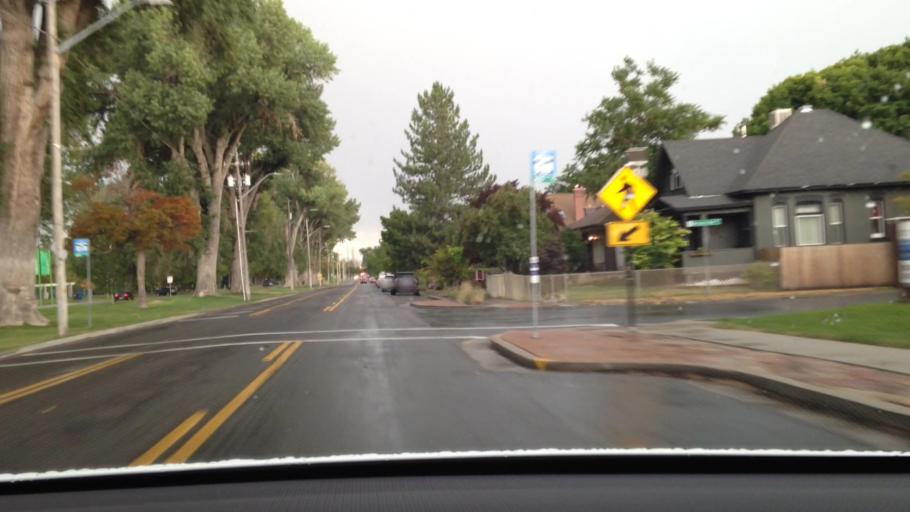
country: US
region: Utah
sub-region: Salt Lake County
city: Salt Lake City
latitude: 40.7467
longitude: -111.8768
